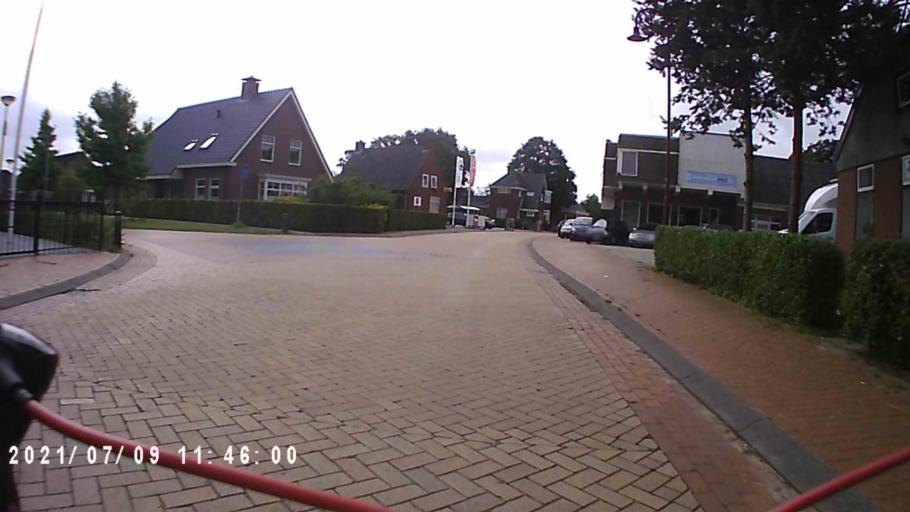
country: NL
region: Groningen
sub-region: Gemeente Slochteren
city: Slochteren
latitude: 53.1953
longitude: 6.8737
